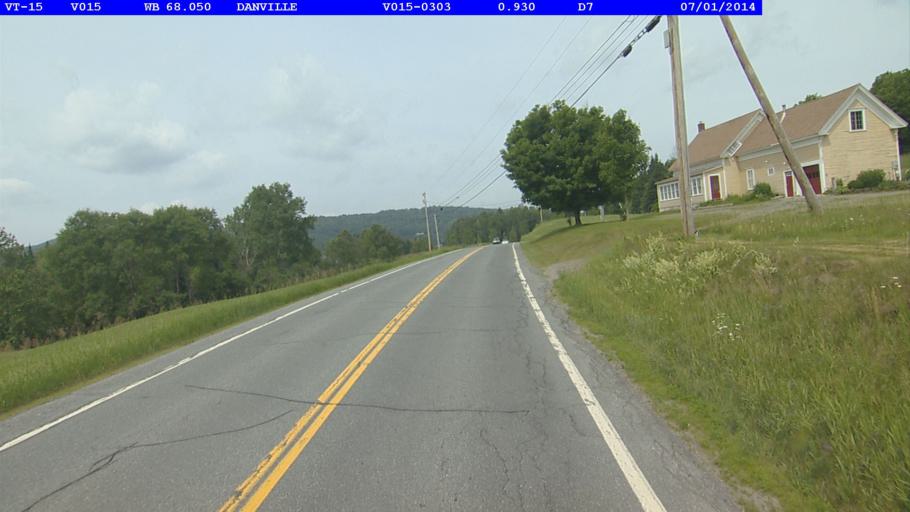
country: US
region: Vermont
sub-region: Caledonia County
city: Hardwick
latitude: 44.4114
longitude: -72.2123
